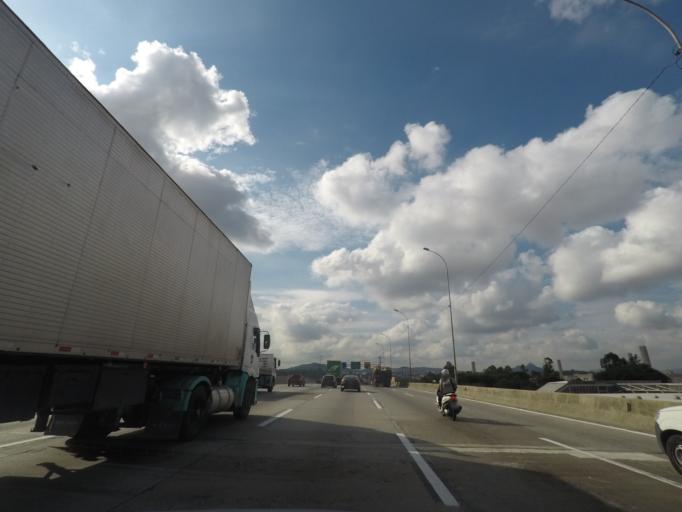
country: BR
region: Sao Paulo
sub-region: Carapicuiba
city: Carapicuiba
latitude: -23.5243
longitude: -46.8165
